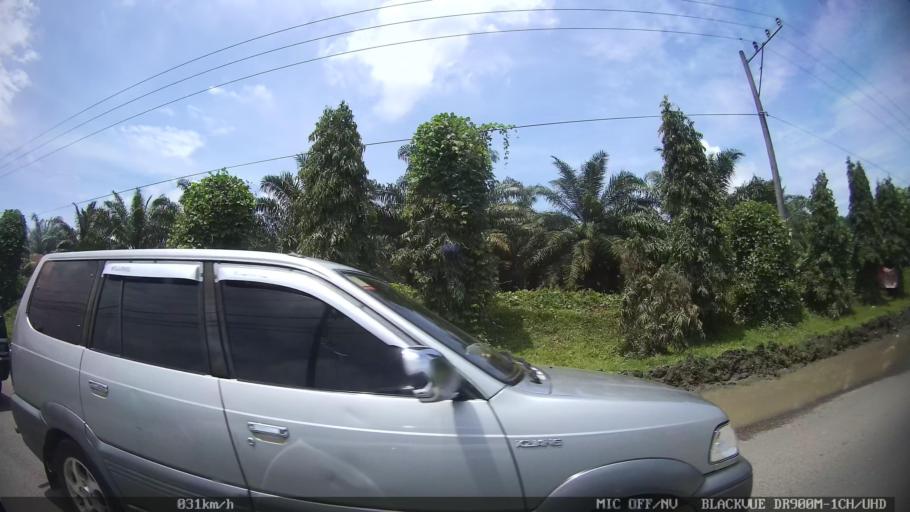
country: ID
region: North Sumatra
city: Perbaungan
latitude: 3.5353
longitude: 98.8850
